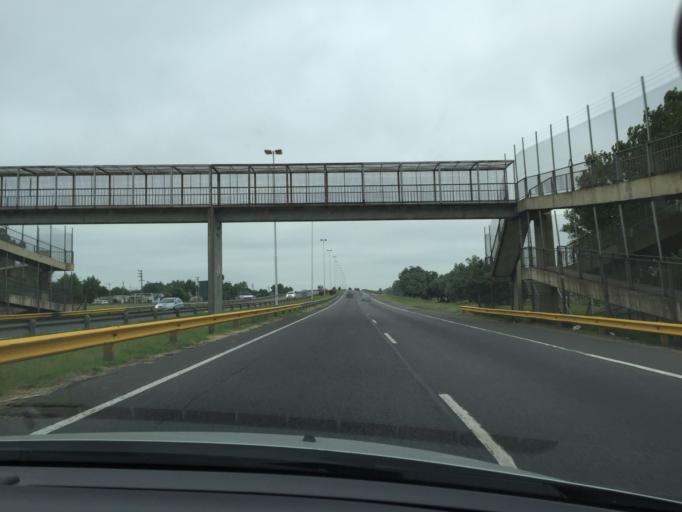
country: AR
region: Buenos Aires
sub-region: Partido de Ezeiza
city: Ezeiza
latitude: -34.8468
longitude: -58.5383
